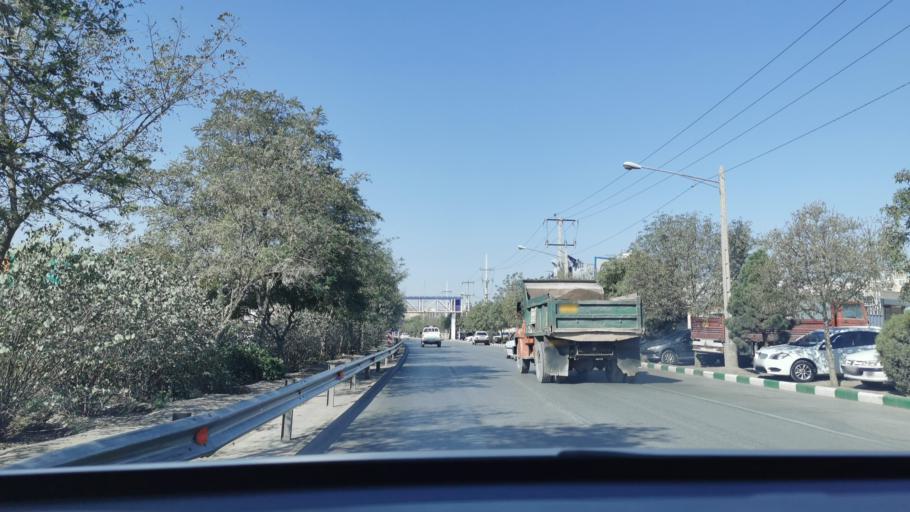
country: IR
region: Razavi Khorasan
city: Mashhad
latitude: 36.3502
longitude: 59.5726
